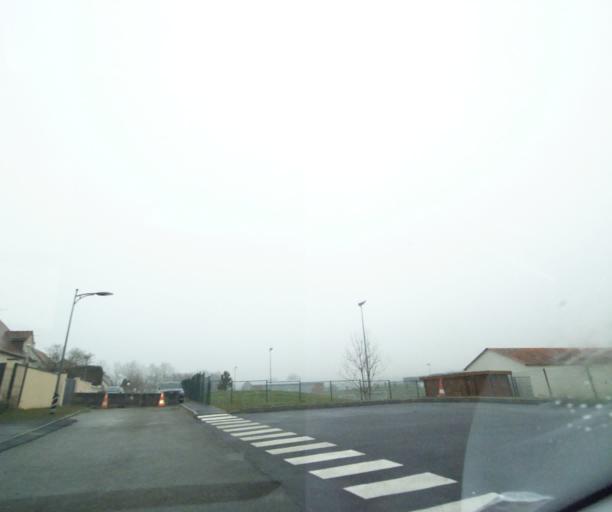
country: FR
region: Ile-de-France
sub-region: Departement de Seine-et-Marne
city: Othis
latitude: 49.0668
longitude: 2.6827
